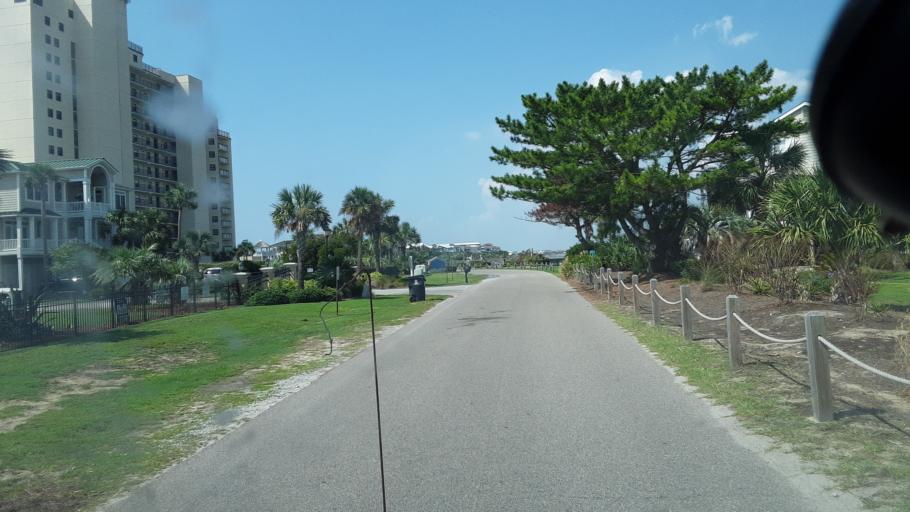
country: US
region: North Carolina
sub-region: Brunswick County
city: Sunset Beach
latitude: 33.8791
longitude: -78.4696
